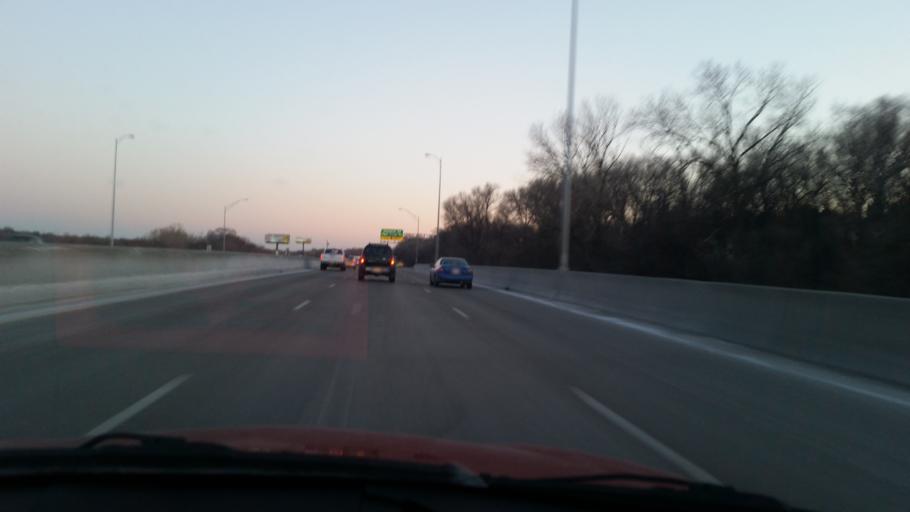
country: US
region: Nebraska
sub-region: Douglas County
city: Omaha
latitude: 41.1948
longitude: -95.9415
